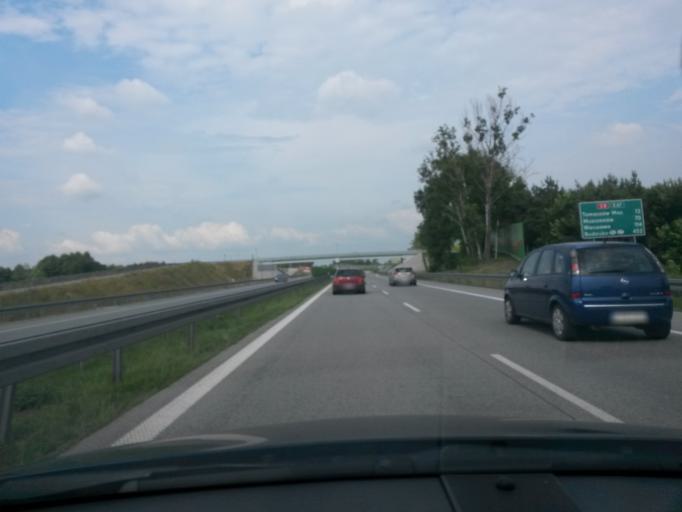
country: PL
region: Lodz Voivodeship
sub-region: Powiat tomaszowski
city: Ujazd
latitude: 51.5192
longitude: 19.9171
